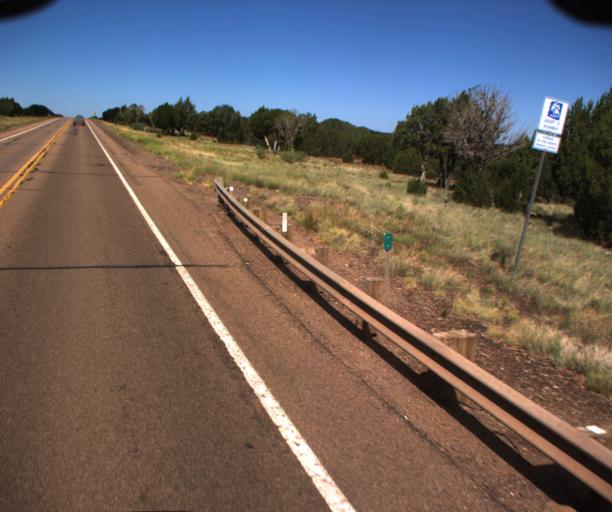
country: US
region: Arizona
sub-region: Navajo County
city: Show Low
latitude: 34.2683
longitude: -109.9379
